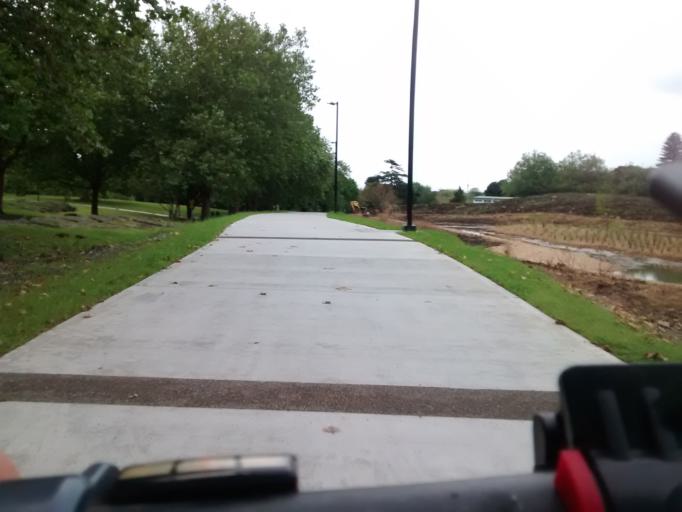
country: NZ
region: Auckland
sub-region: Auckland
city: Rosebank
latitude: -36.8803
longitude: 174.7051
